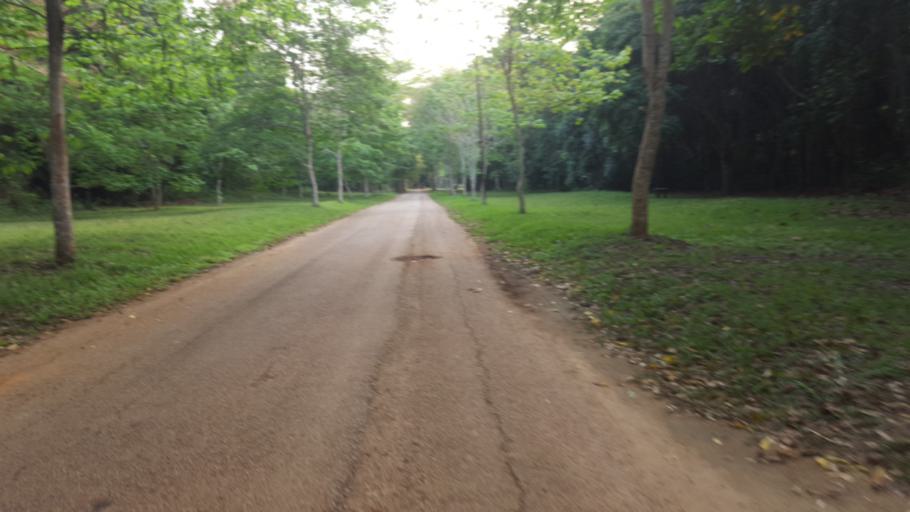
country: CD
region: Bas-Congo
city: Mbanza-Ngungu
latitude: -5.1344
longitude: 15.0771
